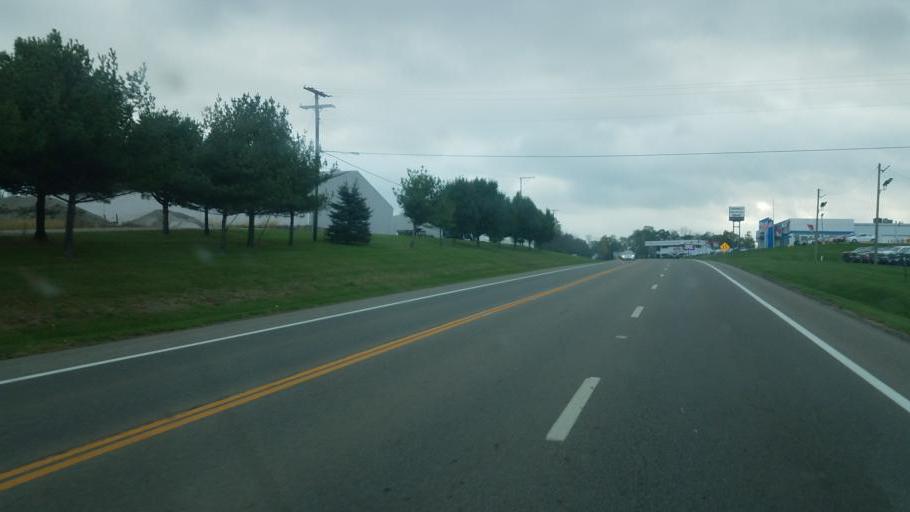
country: US
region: Ohio
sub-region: Holmes County
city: Millersburg
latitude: 40.5561
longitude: -81.8851
